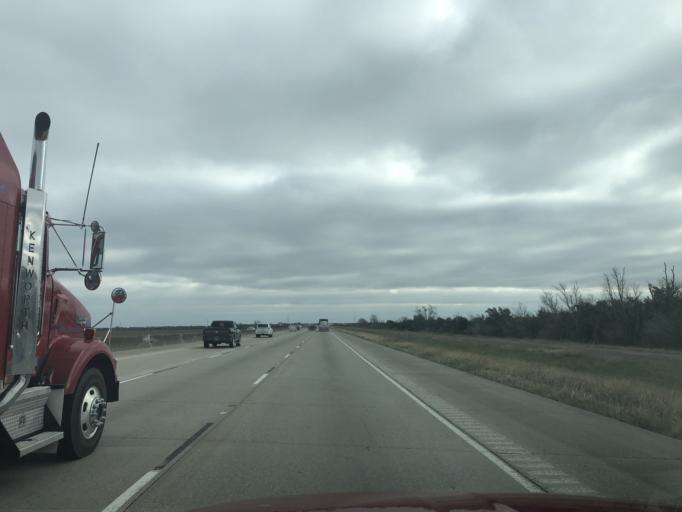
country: US
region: Texas
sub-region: Chambers County
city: Winnie
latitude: 29.8286
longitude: -94.4643
